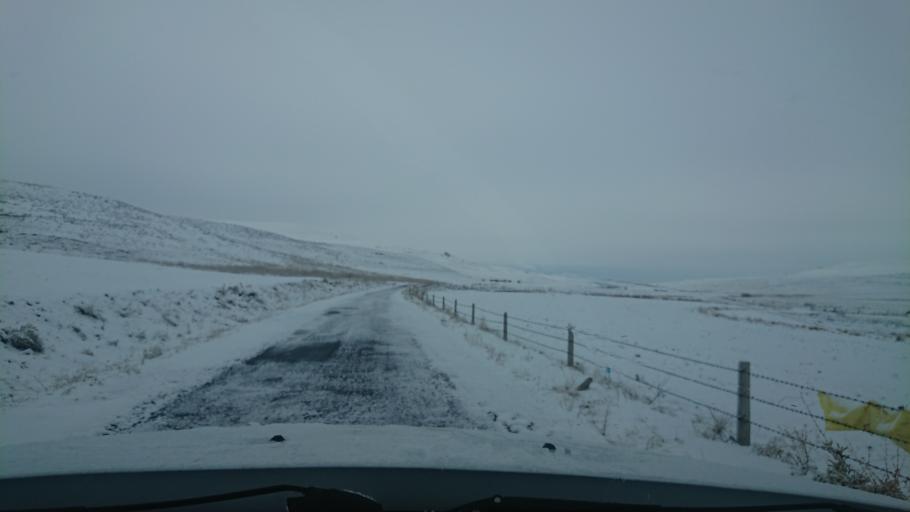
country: TR
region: Aksaray
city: Acipinar
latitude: 38.6813
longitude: 33.8639
